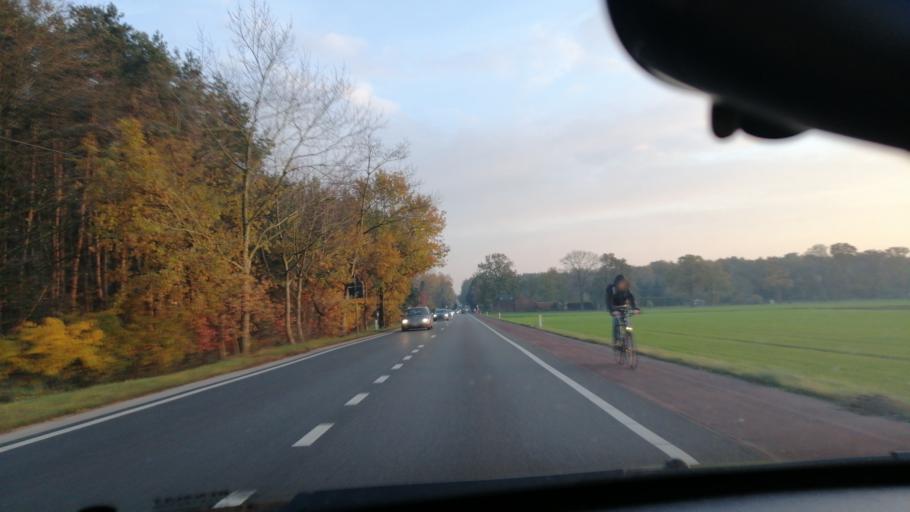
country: BE
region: Flanders
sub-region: Provincie Antwerpen
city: Herentals
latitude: 51.2044
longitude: 4.8194
